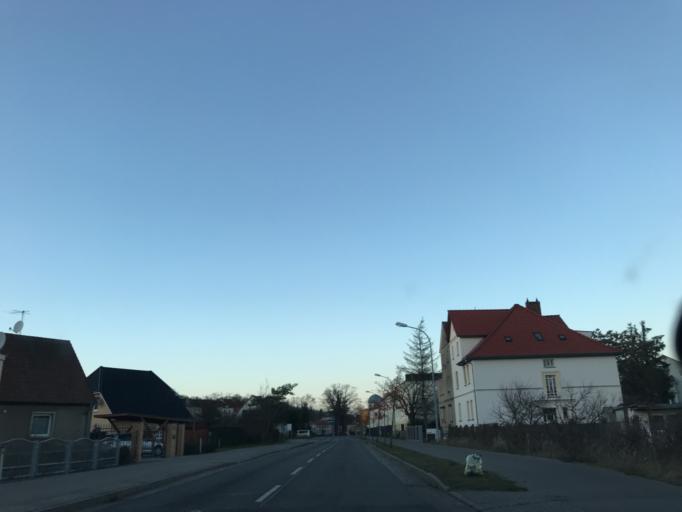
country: DE
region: Brandenburg
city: Rathenow
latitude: 52.5974
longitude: 12.3399
